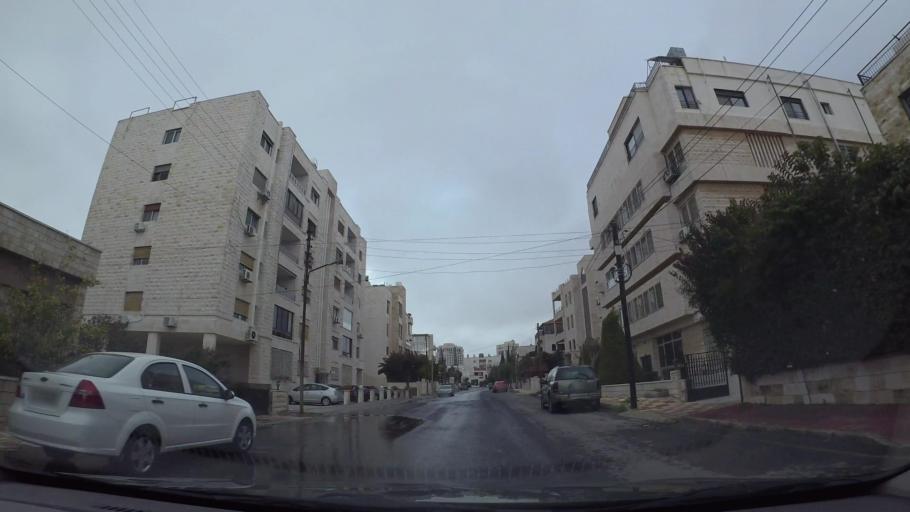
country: JO
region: Amman
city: Wadi as Sir
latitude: 31.9521
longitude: 35.8754
